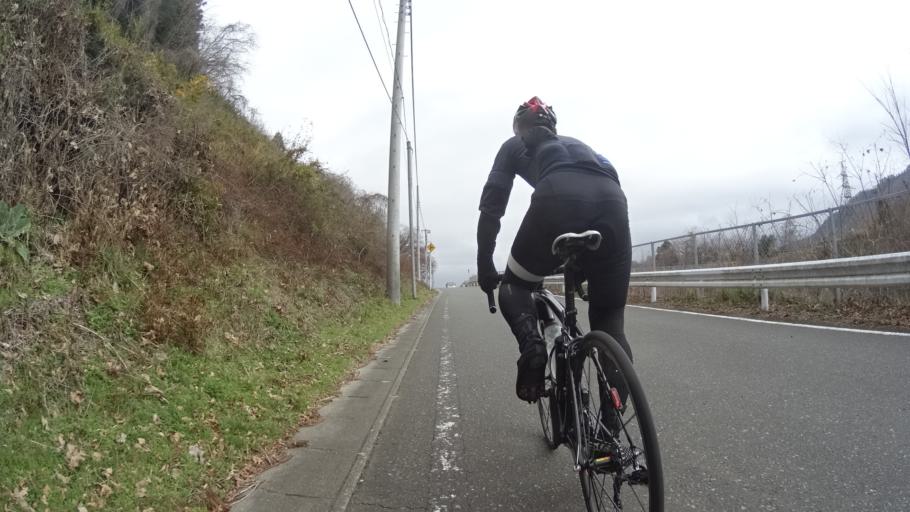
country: JP
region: Yamanashi
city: Otsuki
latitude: 35.6160
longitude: 138.9618
